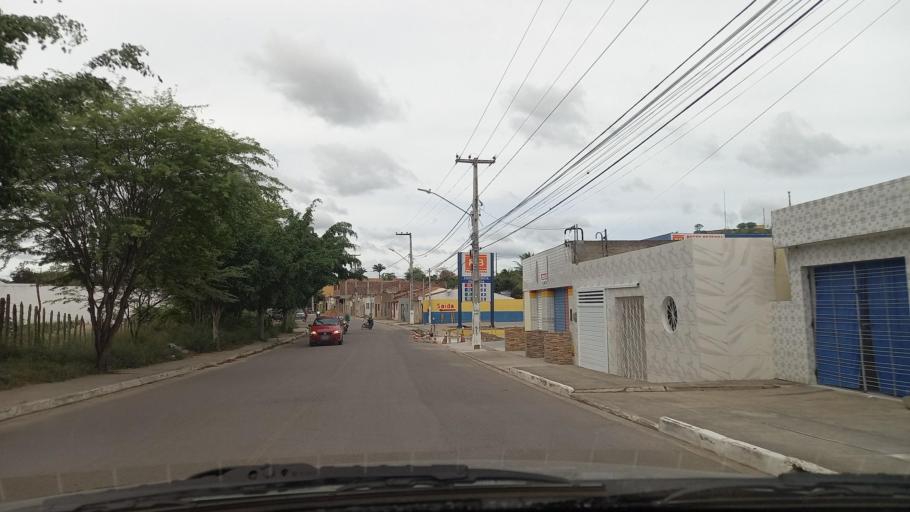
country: BR
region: Pernambuco
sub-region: Gravata
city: Gravata
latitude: -8.2063
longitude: -35.5826
